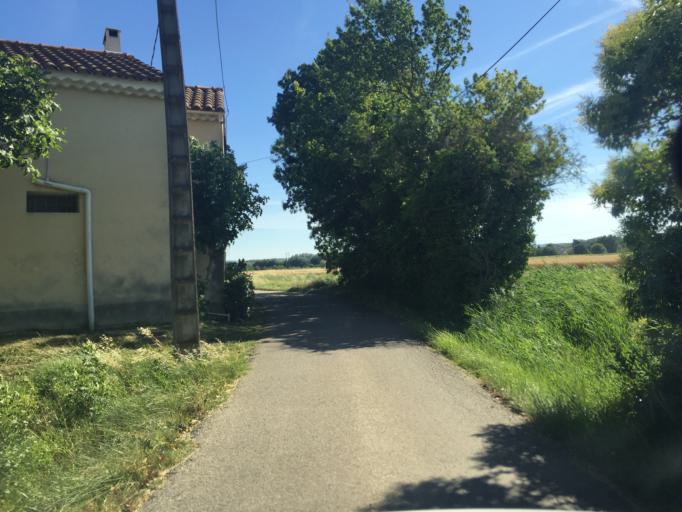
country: FR
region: Provence-Alpes-Cote d'Azur
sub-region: Departement du Vaucluse
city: Caderousse
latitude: 44.1088
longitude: 4.7427
